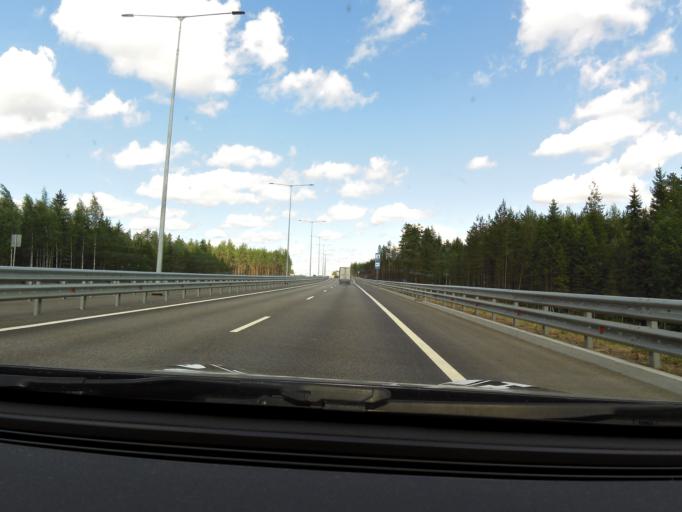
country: RU
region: Tverskaya
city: Krasnomayskiy
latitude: 57.6745
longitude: 34.2279
